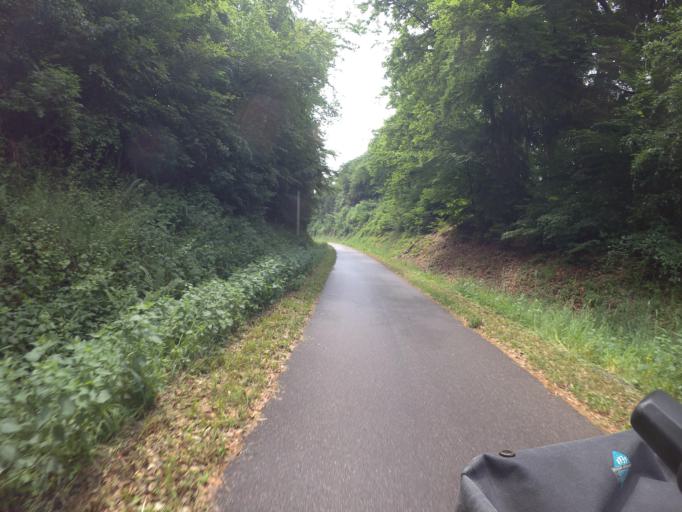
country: DE
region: Rheinland-Pfalz
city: Wittlich
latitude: 50.0092
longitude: 6.8883
